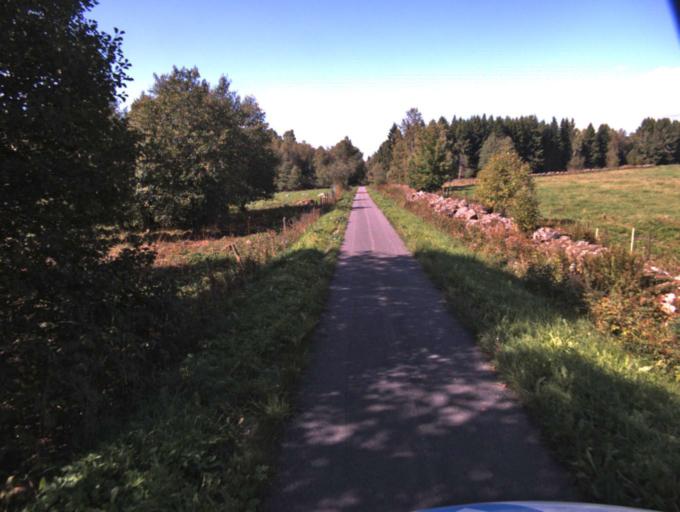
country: SE
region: Vaestra Goetaland
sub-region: Ulricehamns Kommun
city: Ulricehamn
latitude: 57.8034
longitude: 13.3648
